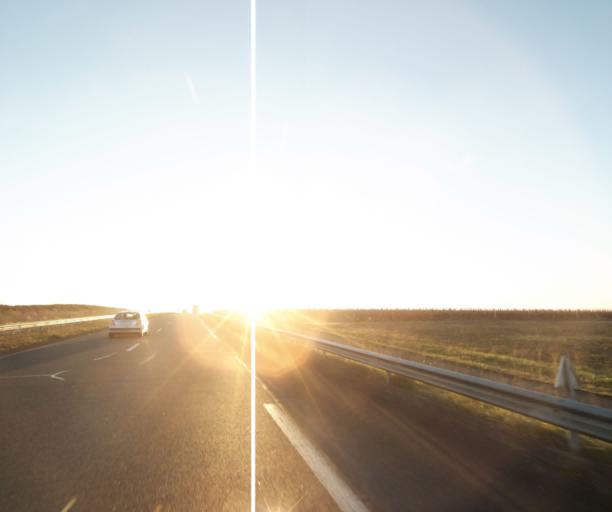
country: FR
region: Poitou-Charentes
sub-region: Departement de la Charente-Maritime
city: Cherac
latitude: 45.7055
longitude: -0.4787
